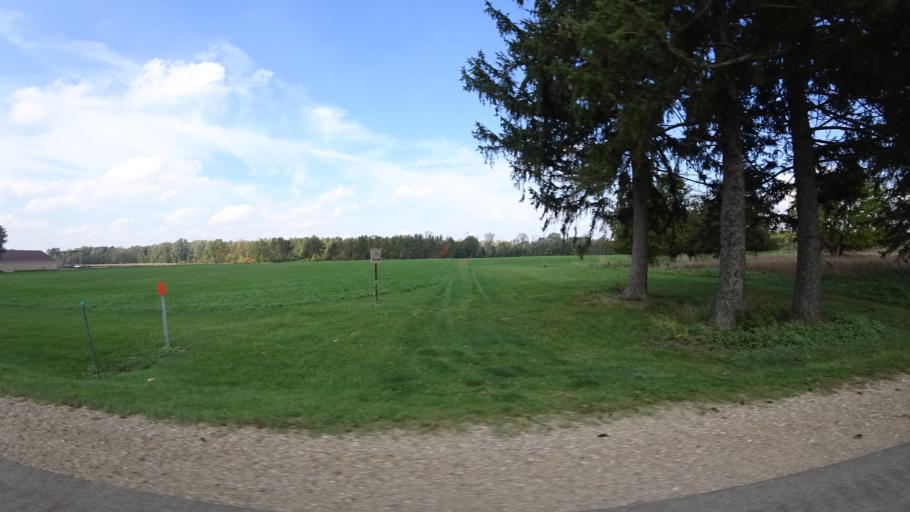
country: US
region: Michigan
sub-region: Saint Joseph County
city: Centreville
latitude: 42.0061
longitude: -85.5253
